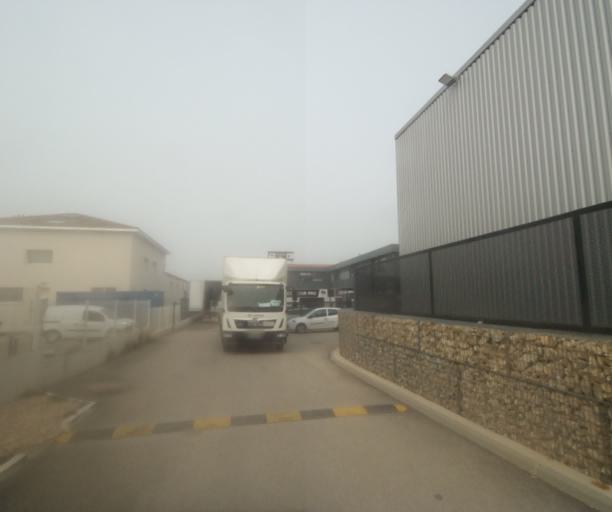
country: FR
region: Provence-Alpes-Cote d'Azur
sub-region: Departement des Bouches-du-Rhone
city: Eguilles
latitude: 43.5473
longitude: 5.3586
